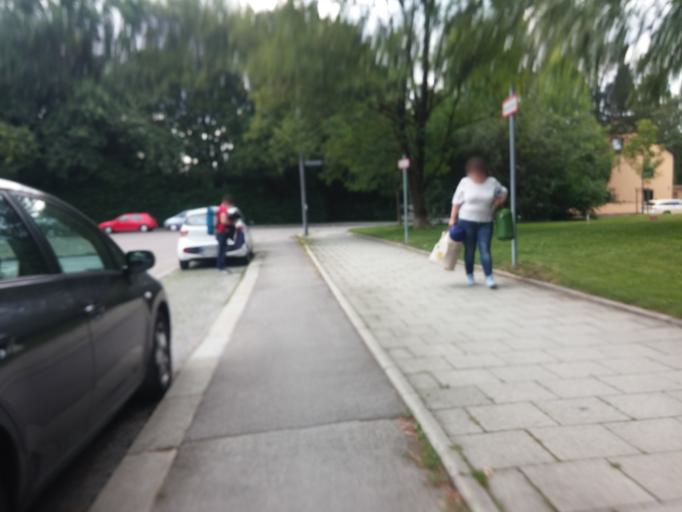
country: DE
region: Bavaria
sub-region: Upper Bavaria
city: Bogenhausen
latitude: 48.1591
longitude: 11.6396
